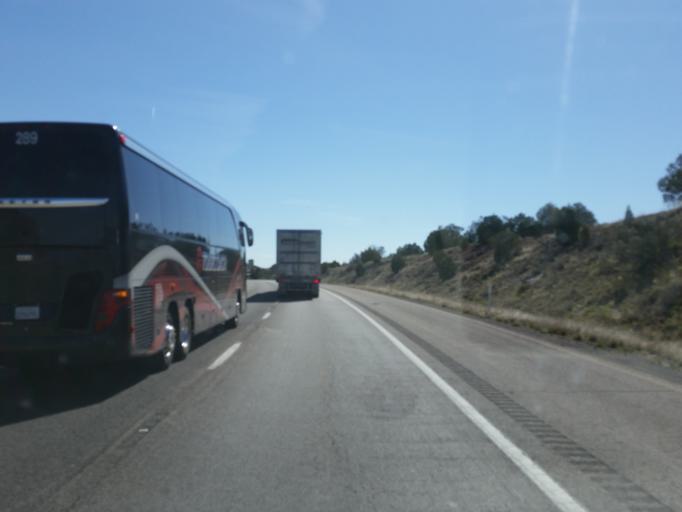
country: US
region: Arizona
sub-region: Mohave County
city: Peach Springs
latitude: 35.2859
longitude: -113.0952
